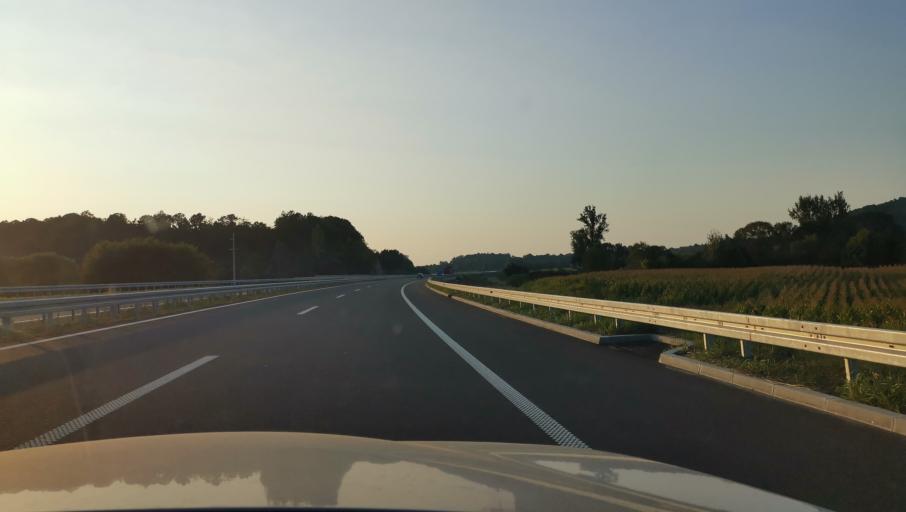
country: RS
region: Central Serbia
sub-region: Kolubarski Okrug
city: Lajkovac
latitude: 44.3365
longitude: 20.2008
